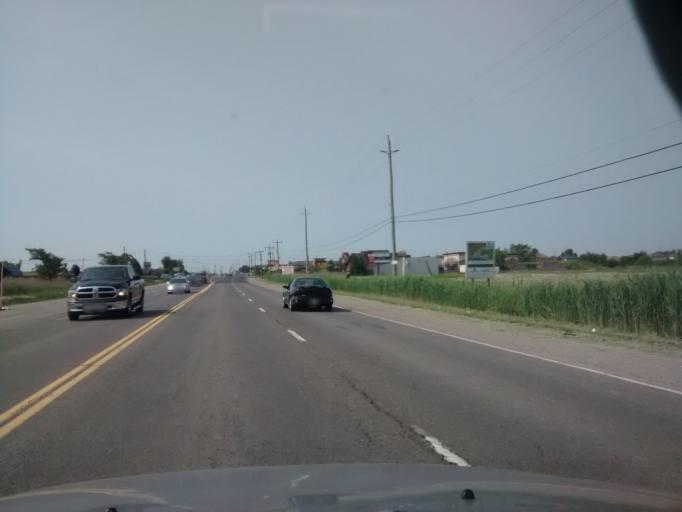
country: CA
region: Ontario
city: Hamilton
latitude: 43.1849
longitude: -79.7716
